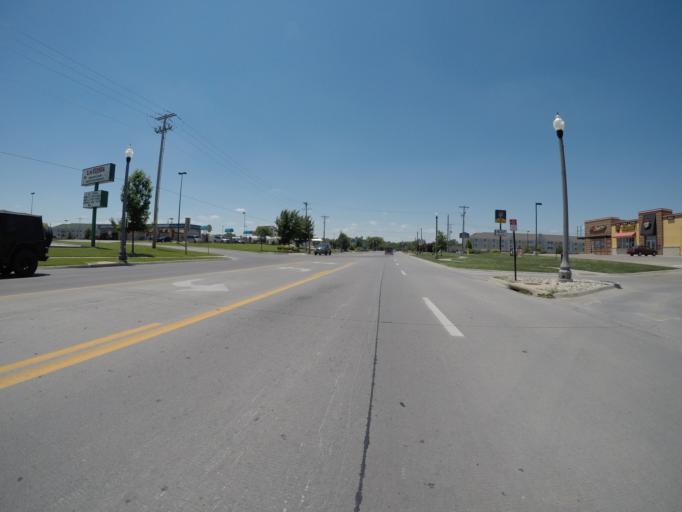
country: US
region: Kansas
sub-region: Geary County
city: Junction City
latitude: 39.0218
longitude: -96.8219
